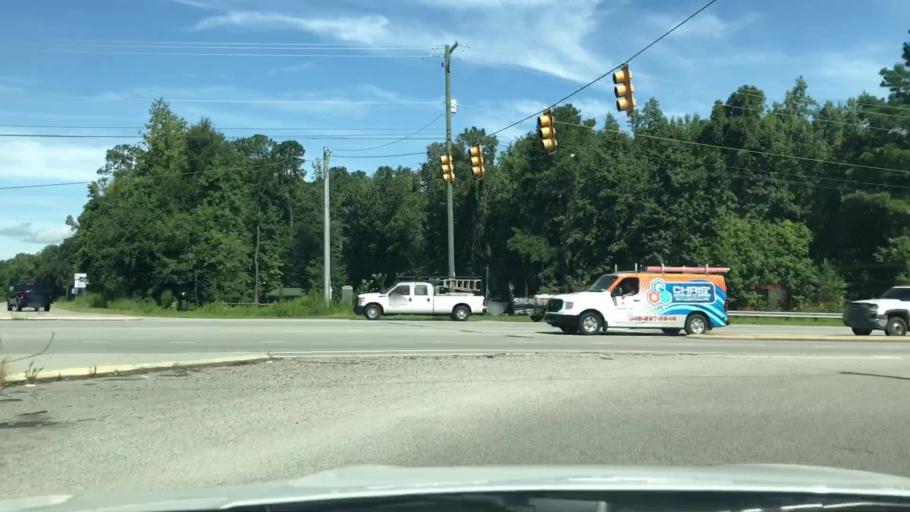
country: US
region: South Carolina
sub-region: Dorchester County
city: Centerville
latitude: 32.9482
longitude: -80.2052
